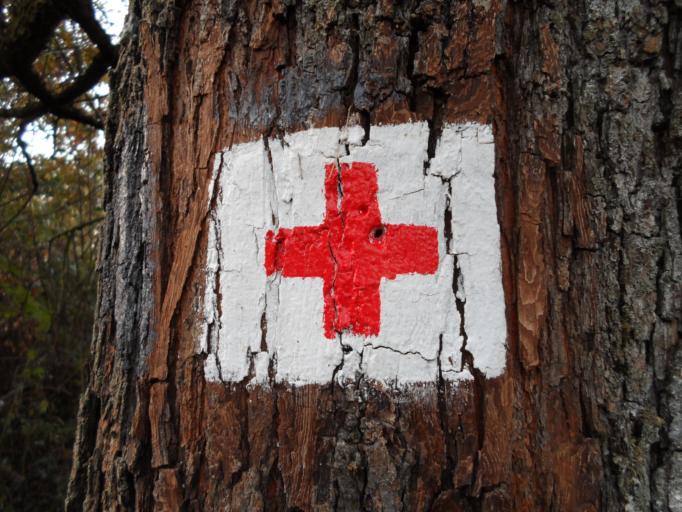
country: HU
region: Veszprem
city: Herend
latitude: 47.1871
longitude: 17.6900
